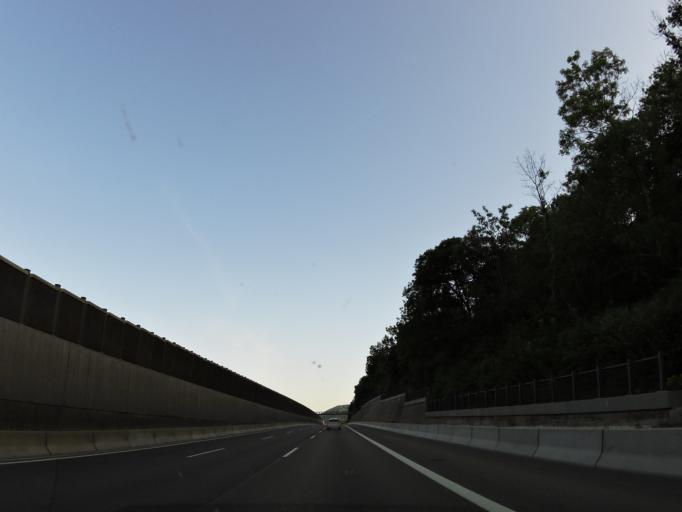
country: DE
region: Baden-Wuerttemberg
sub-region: Regierungsbezirk Stuttgart
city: Gruibingen
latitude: 48.5957
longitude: 9.6466
